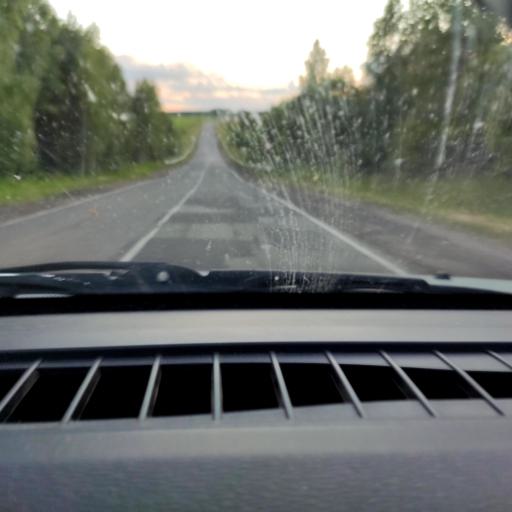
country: RU
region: Perm
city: Orda
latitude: 57.3309
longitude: 56.7157
